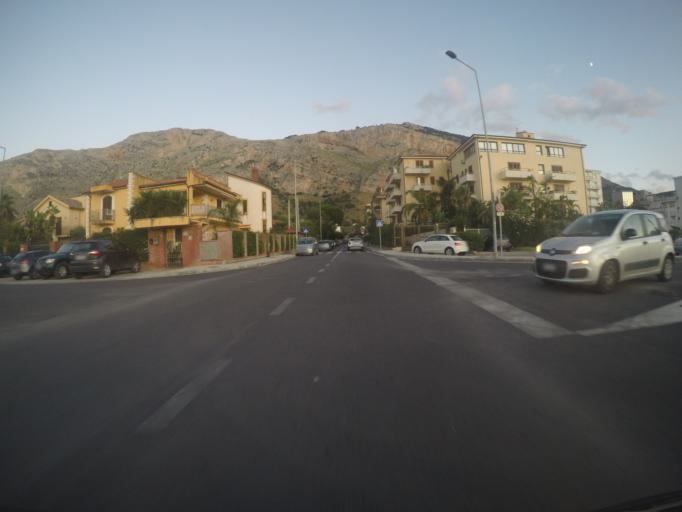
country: IT
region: Sicily
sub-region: Palermo
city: Capaci
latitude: 38.1809
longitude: 13.2417
